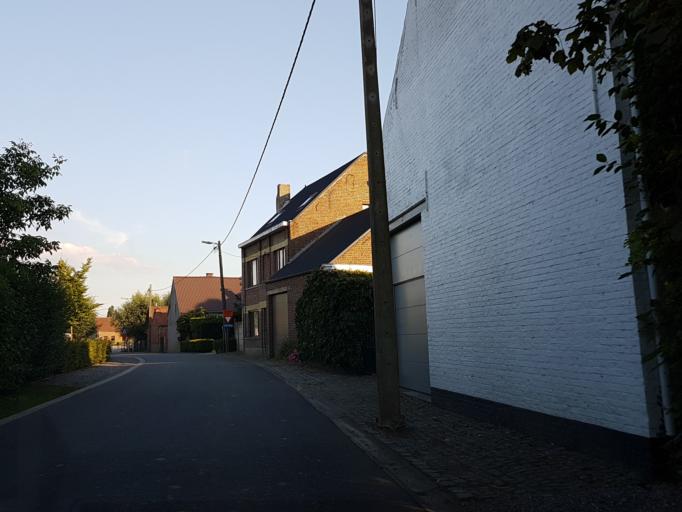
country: BE
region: Flanders
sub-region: Provincie Vlaams-Brabant
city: Merchtem
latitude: 50.9441
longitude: 4.2181
